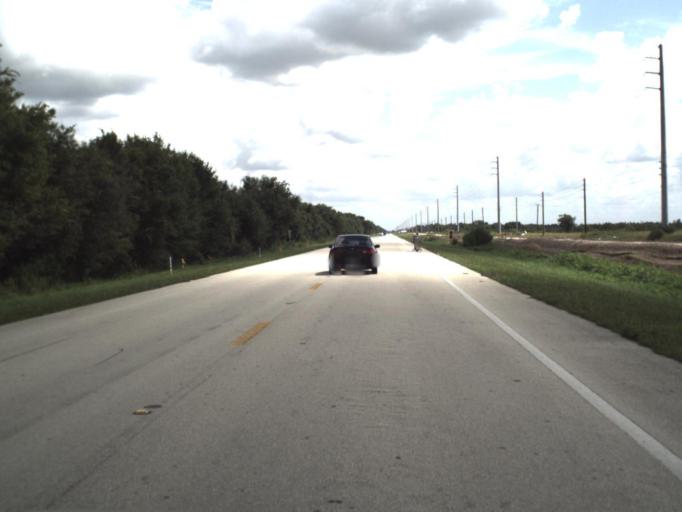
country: US
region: Florida
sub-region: DeSoto County
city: Nocatee
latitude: 27.0945
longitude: -81.9445
